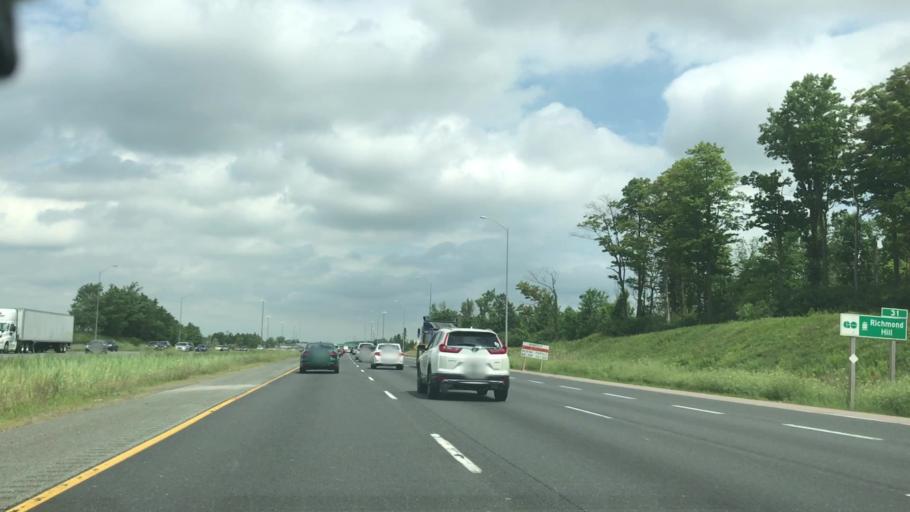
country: CA
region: Ontario
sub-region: York
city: Richmond Hill
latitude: 43.8706
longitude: -79.3765
